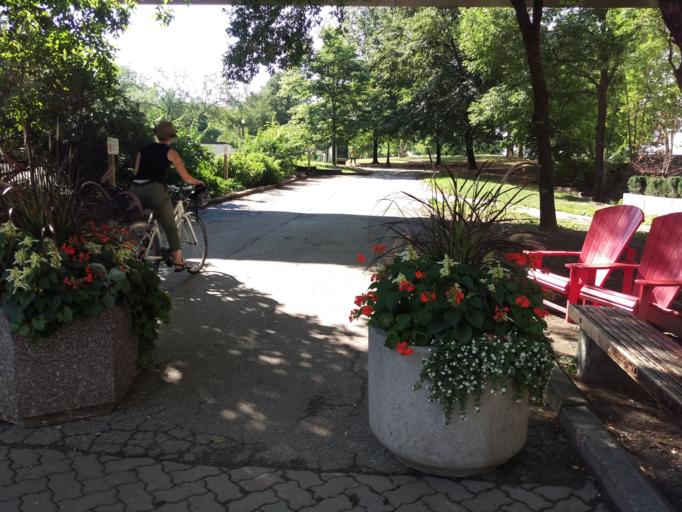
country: CA
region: Ontario
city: Toronto
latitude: 43.6410
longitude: -79.3765
